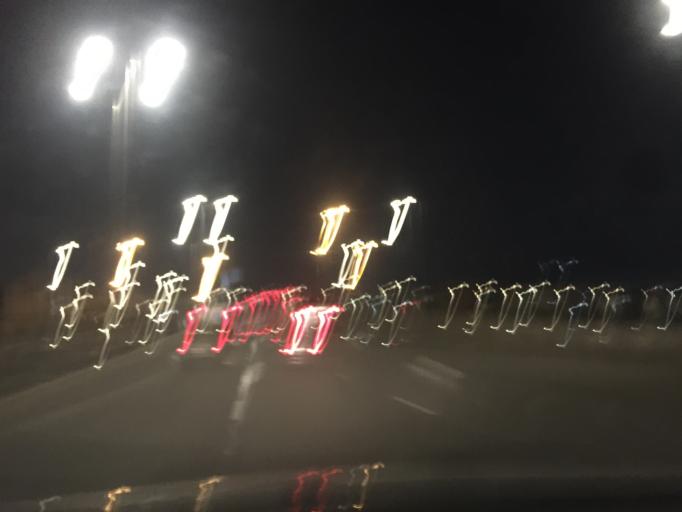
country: JO
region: Amman
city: Wadi as Sir
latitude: 31.9426
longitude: 35.8493
